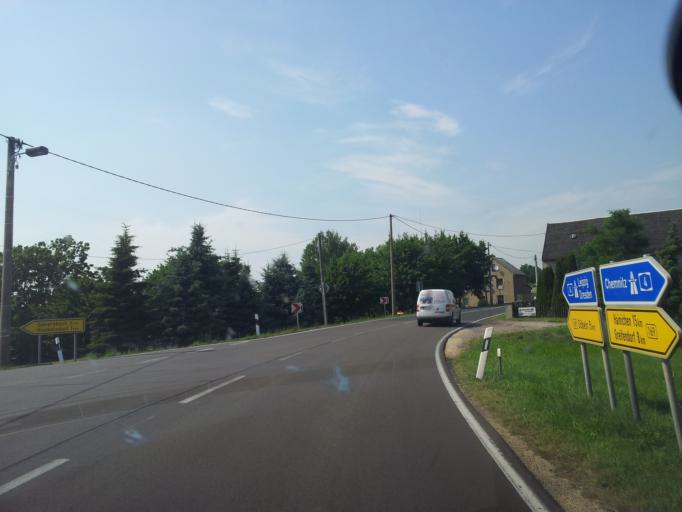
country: DE
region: Saxony
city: Ebersbach
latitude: 51.0914
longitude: 13.1017
